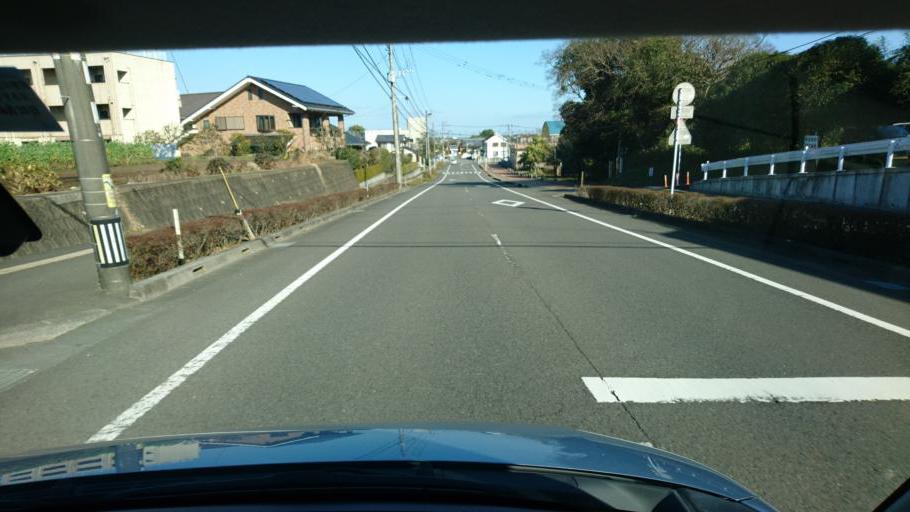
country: JP
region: Miyazaki
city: Miyazaki-shi
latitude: 31.8324
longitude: 131.4334
